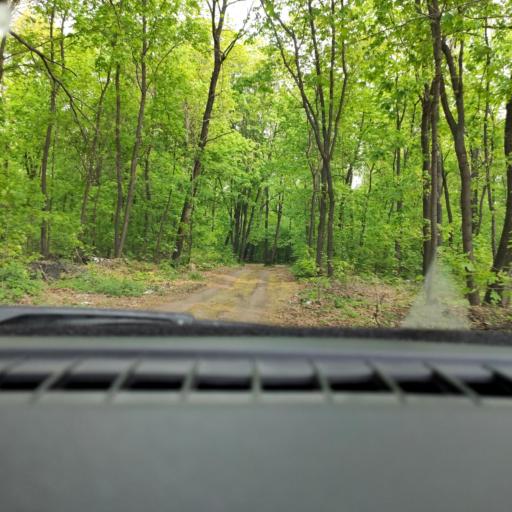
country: RU
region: Samara
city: Bereza
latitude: 53.5070
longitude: 50.1263
